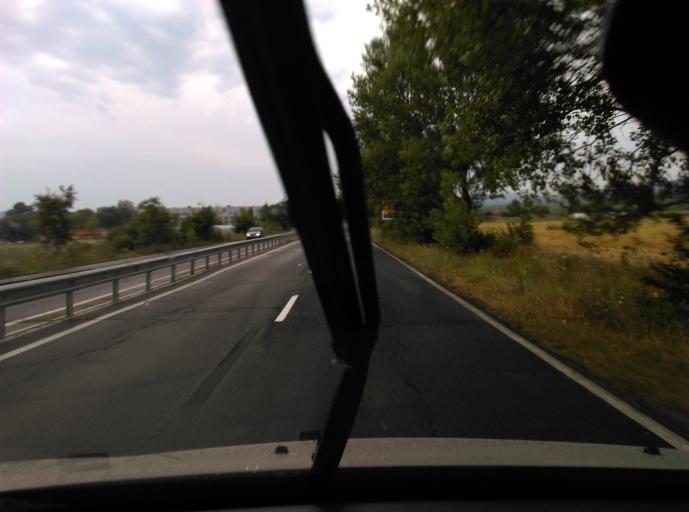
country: BG
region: Burgas
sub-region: Obshtina Sozopol
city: Chernomorets
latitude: 42.4255
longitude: 27.6409
